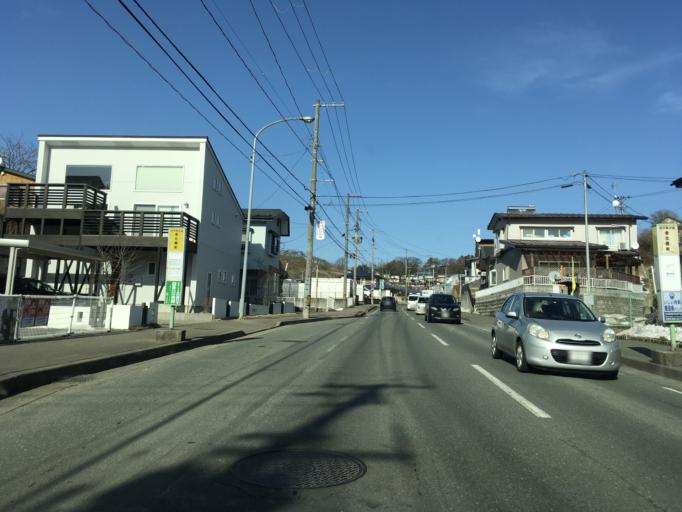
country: JP
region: Iwate
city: Morioka-shi
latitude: 39.7200
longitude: 141.1550
